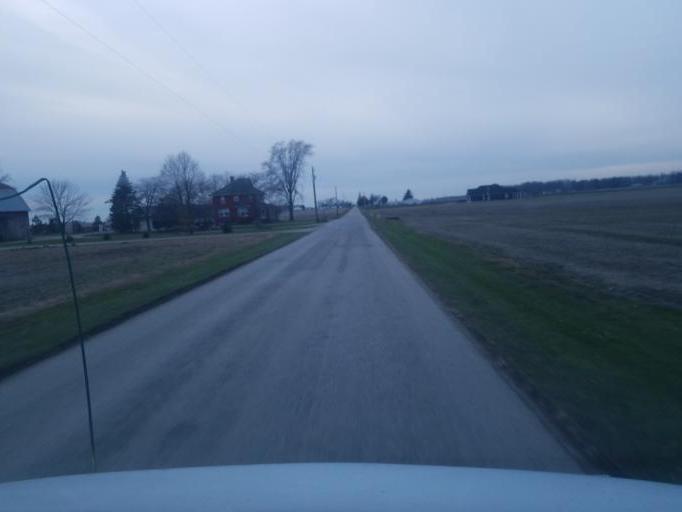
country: US
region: Indiana
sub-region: Adams County
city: Decatur
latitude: 40.7888
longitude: -84.9244
